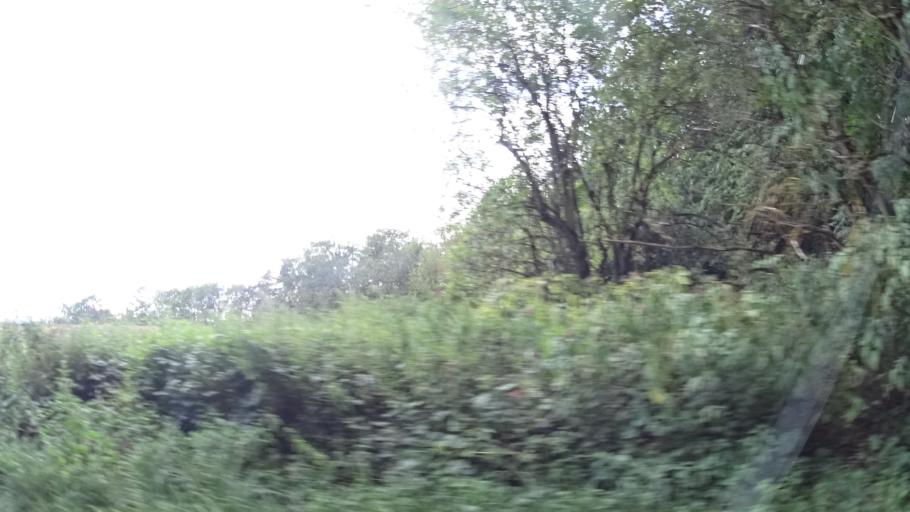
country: DE
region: Thuringia
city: Hildburghausen
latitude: 50.3819
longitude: 10.7454
